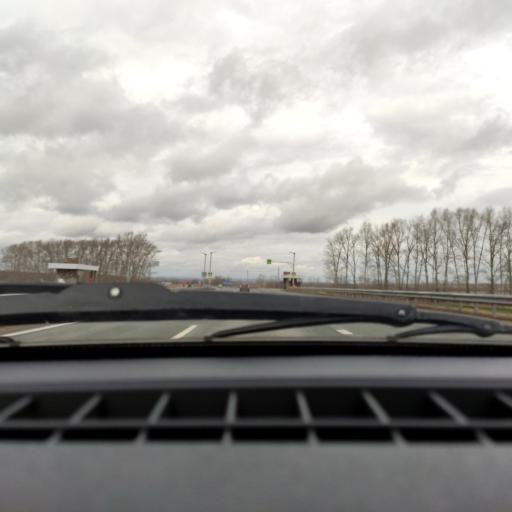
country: RU
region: Bashkortostan
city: Asanovo
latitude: 54.9576
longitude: 55.5856
